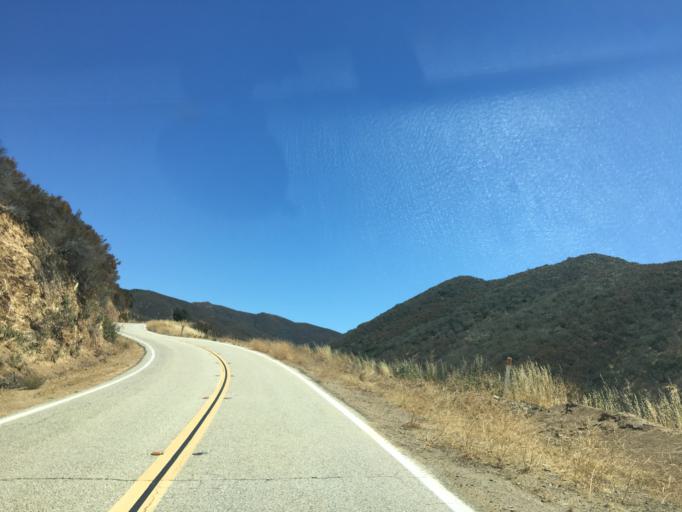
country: US
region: California
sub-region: Los Angeles County
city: Green Valley
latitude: 34.5979
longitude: -118.3852
